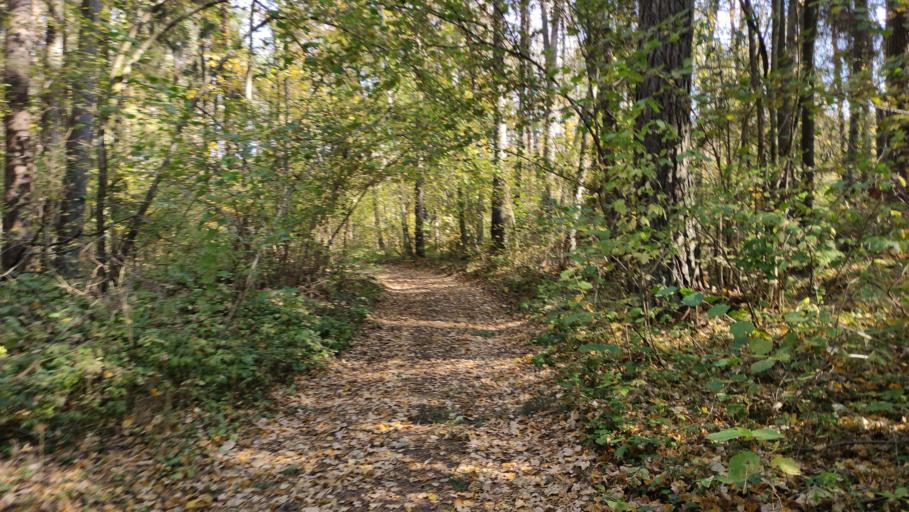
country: LT
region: Alytaus apskritis
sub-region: Alytus
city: Alytus
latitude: 54.3701
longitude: 24.0905
